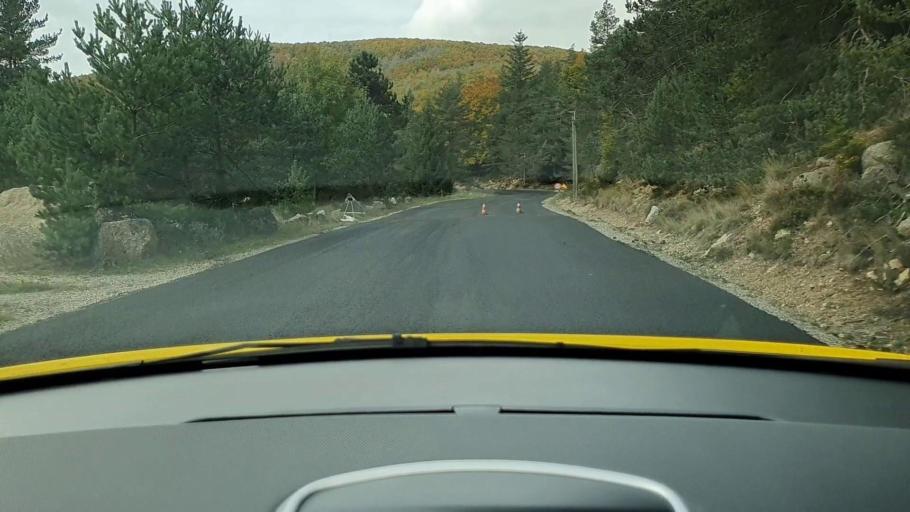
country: FR
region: Languedoc-Roussillon
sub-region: Departement du Gard
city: Valleraugue
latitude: 44.0822
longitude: 3.5403
